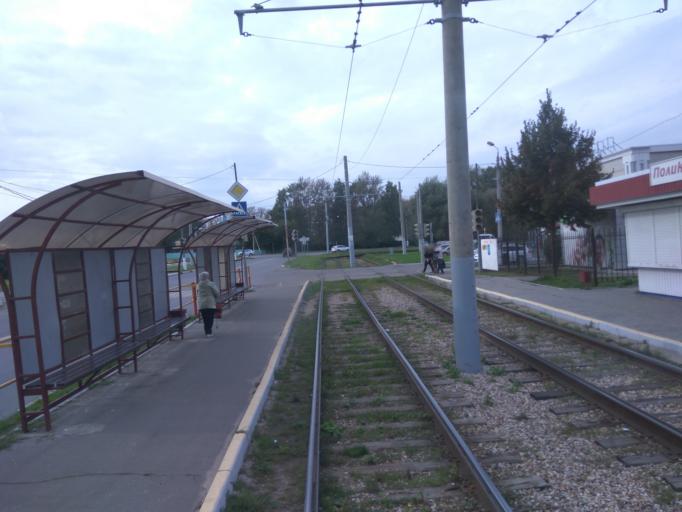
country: RU
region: Moskovskaya
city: Kolomna
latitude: 55.0667
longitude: 38.7545
